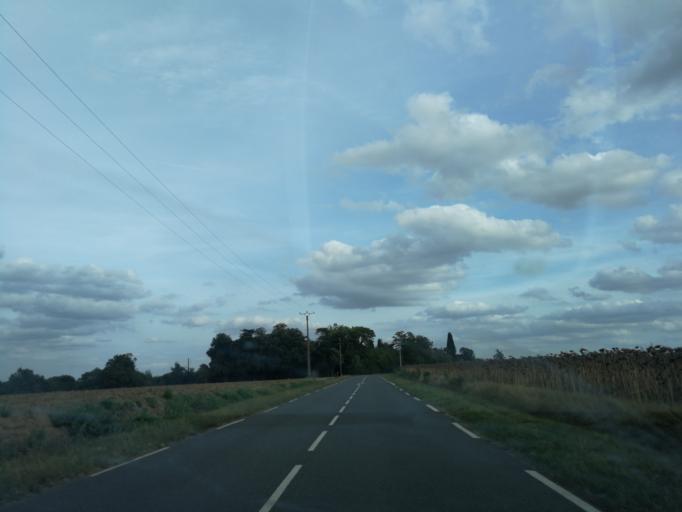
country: FR
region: Midi-Pyrenees
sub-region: Departement de la Haute-Garonne
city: Flourens
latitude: 43.5960
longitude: 1.5537
